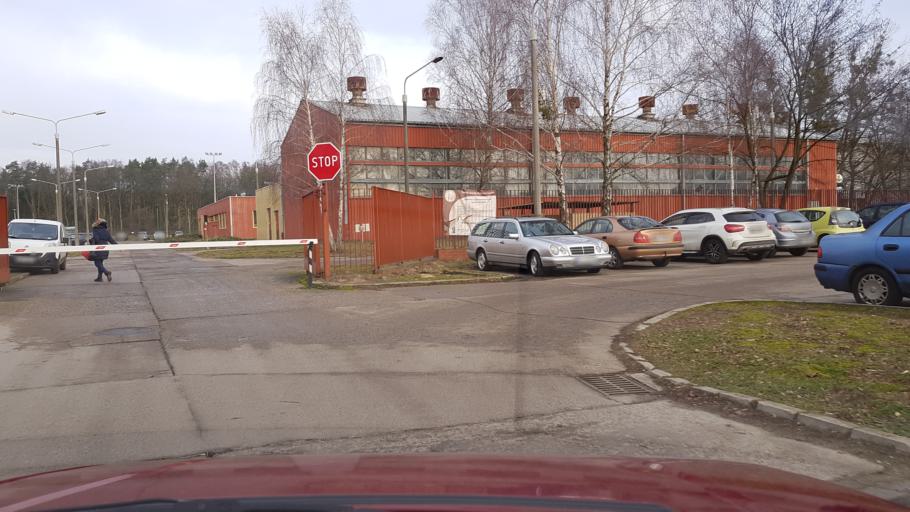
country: PL
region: West Pomeranian Voivodeship
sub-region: Powiat policki
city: Police
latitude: 53.5469
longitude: 14.5628
